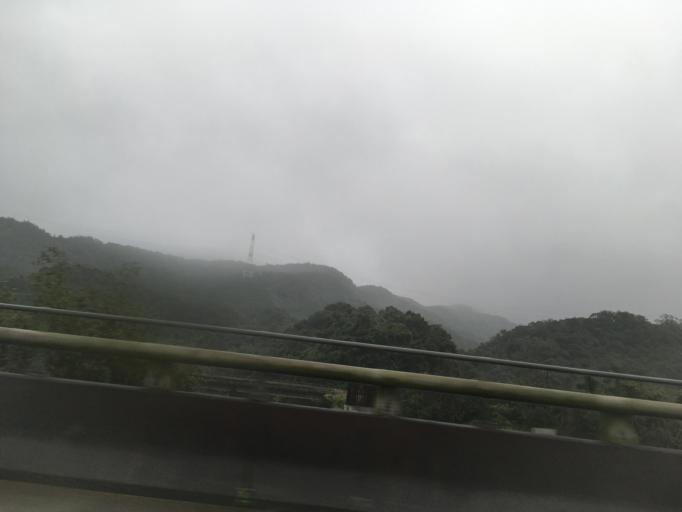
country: TW
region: Taiwan
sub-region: Keelung
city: Keelung
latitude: 25.0237
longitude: 121.8866
